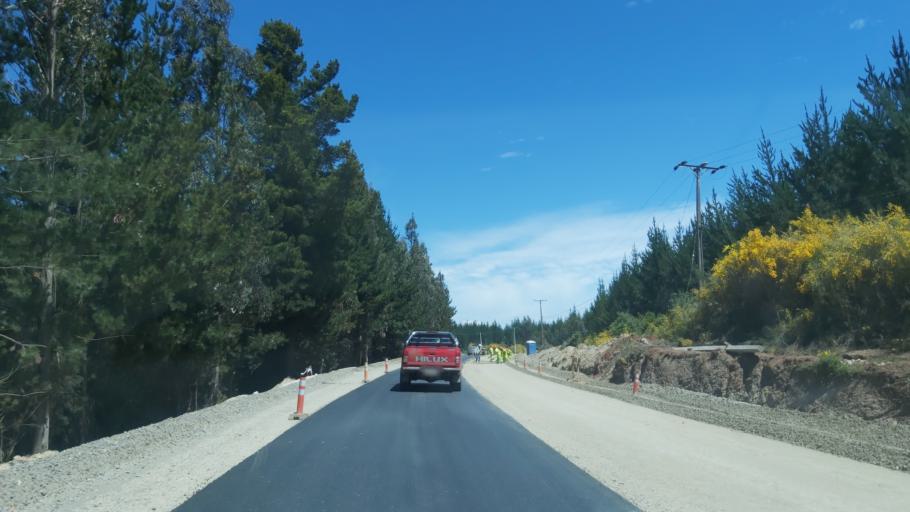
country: CL
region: Maule
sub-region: Provincia de Talca
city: Constitucion
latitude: -35.3812
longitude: -72.4209
